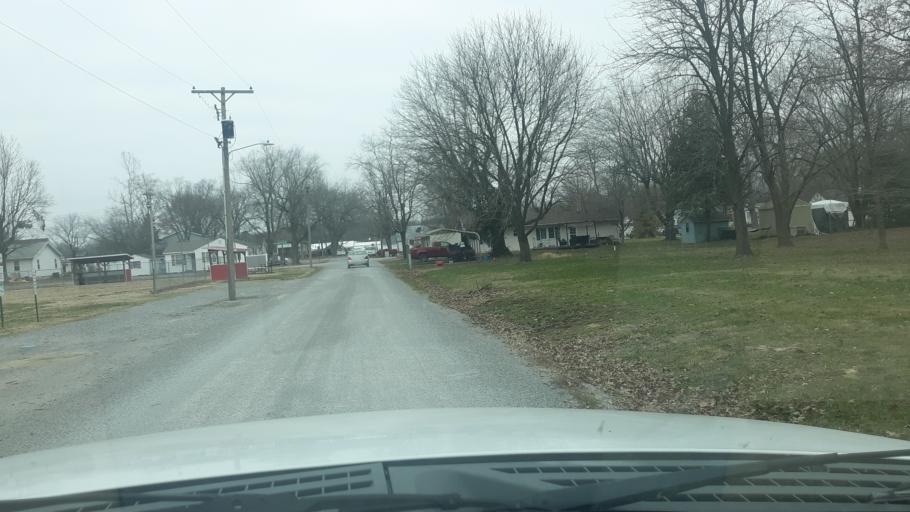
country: US
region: Illinois
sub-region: Saline County
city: Harrisburg
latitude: 37.8382
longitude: -88.6093
